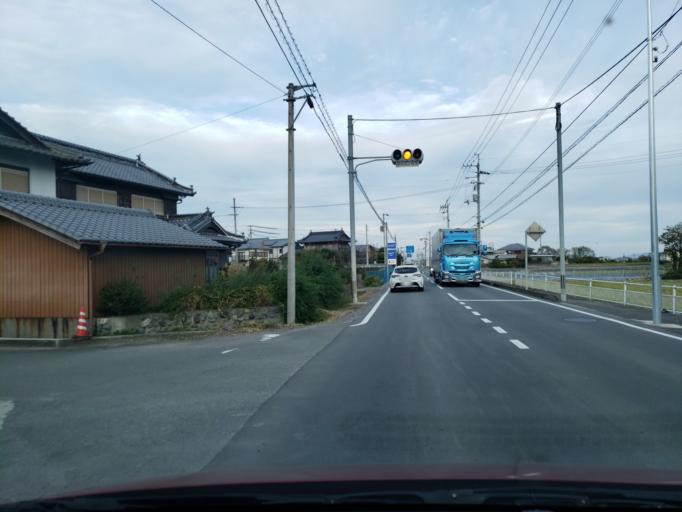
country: JP
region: Tokushima
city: Kamojimacho-jogejima
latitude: 34.0820
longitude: 134.2690
